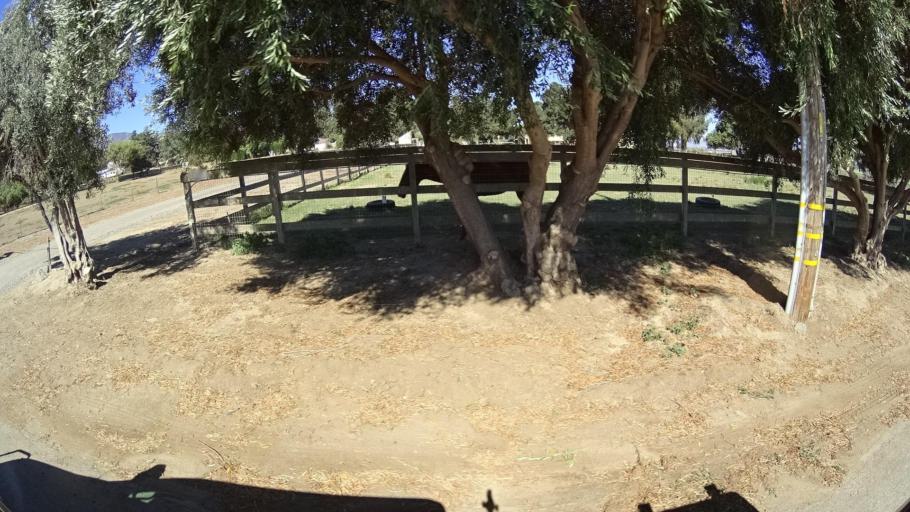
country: US
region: California
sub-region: Monterey County
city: Soledad
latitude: 36.3894
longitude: -121.3606
